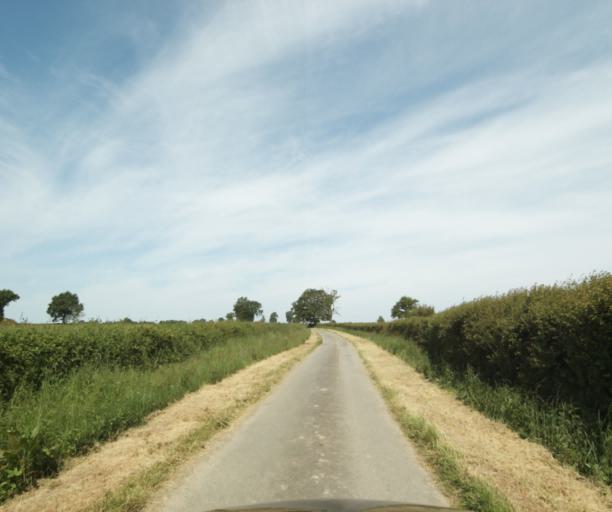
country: FR
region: Bourgogne
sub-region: Departement de Saone-et-Loire
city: Palinges
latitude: 46.5623
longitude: 4.1730
